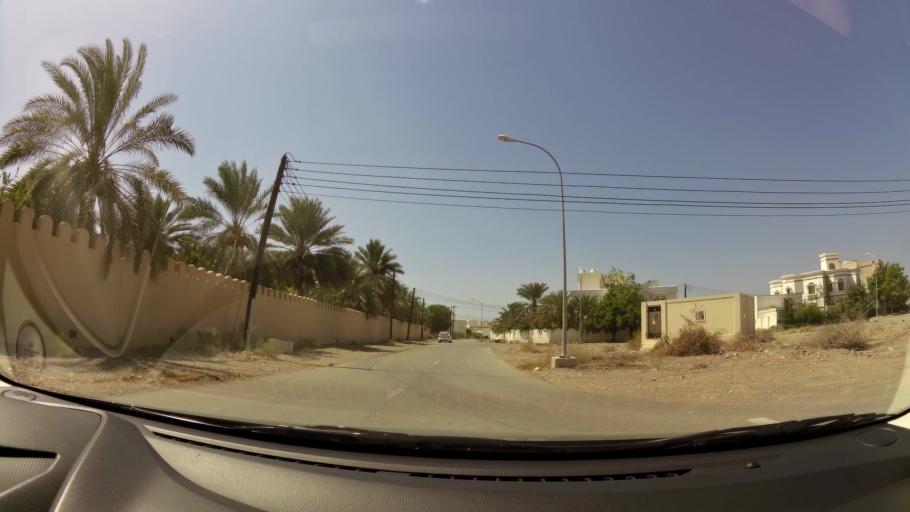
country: OM
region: Muhafazat Masqat
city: As Sib al Jadidah
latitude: 23.6196
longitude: 58.2192
